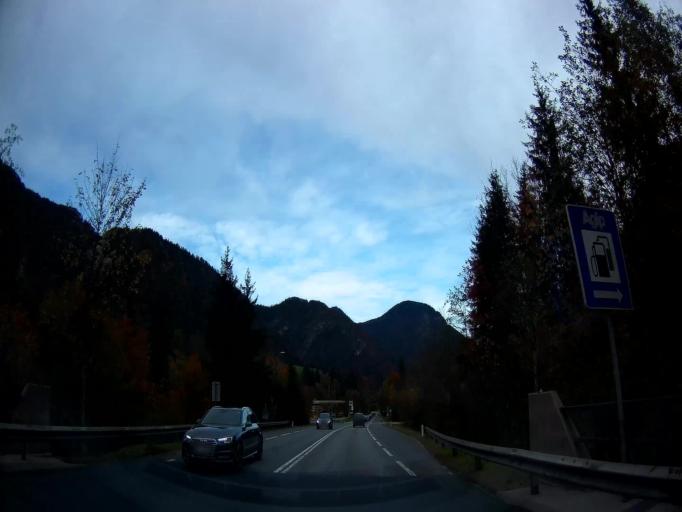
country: AT
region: Salzburg
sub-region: Politischer Bezirk Zell am See
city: Unken
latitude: 47.6558
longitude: 12.7420
